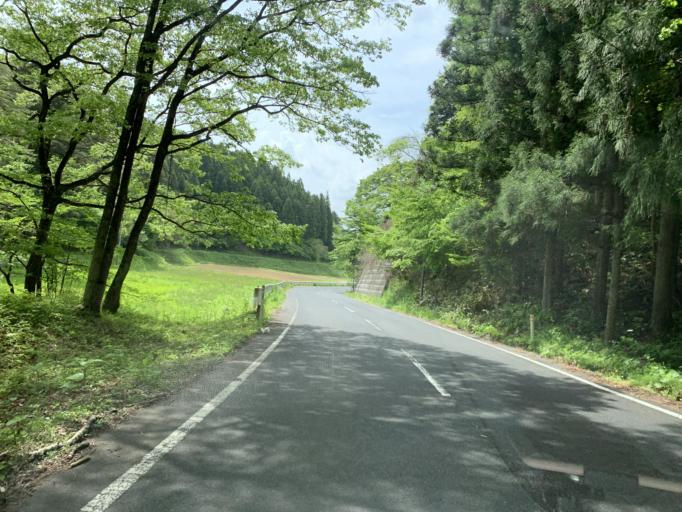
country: JP
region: Iwate
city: Ichinoseki
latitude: 38.8727
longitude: 140.9790
